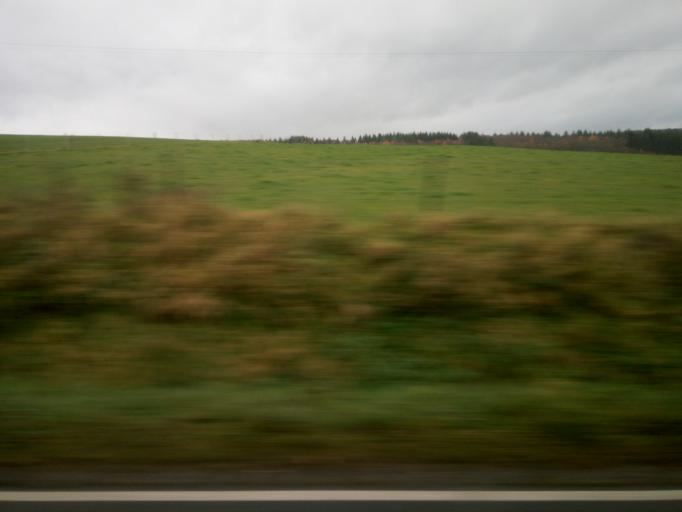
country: DE
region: Rheinland-Pfalz
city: Gentingen
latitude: 49.9149
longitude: 6.2194
